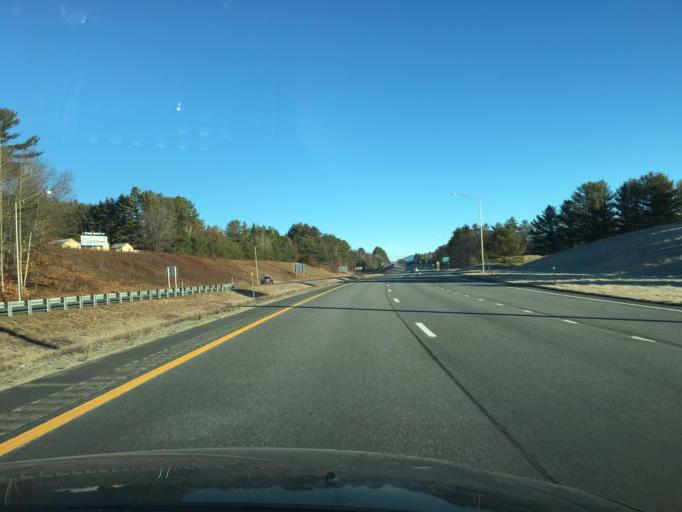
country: US
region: New Hampshire
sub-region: Grafton County
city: Plymouth
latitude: 43.7726
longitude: -71.6824
